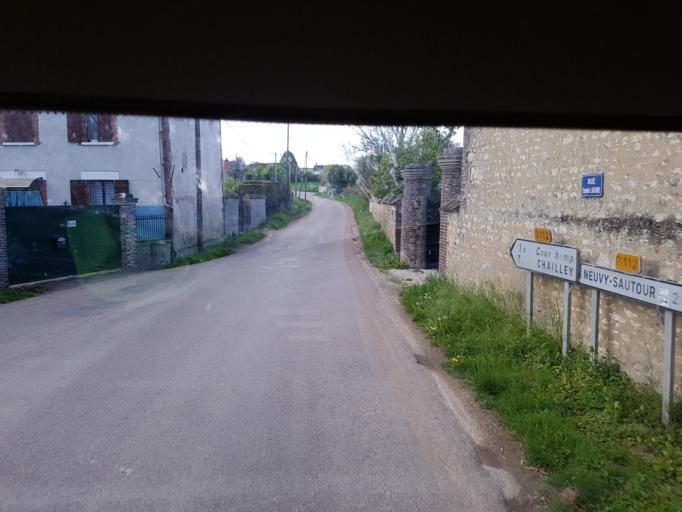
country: FR
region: Bourgogne
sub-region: Departement de l'Yonne
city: Neuvy-Sautour
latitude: 48.0534
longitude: 3.7720
